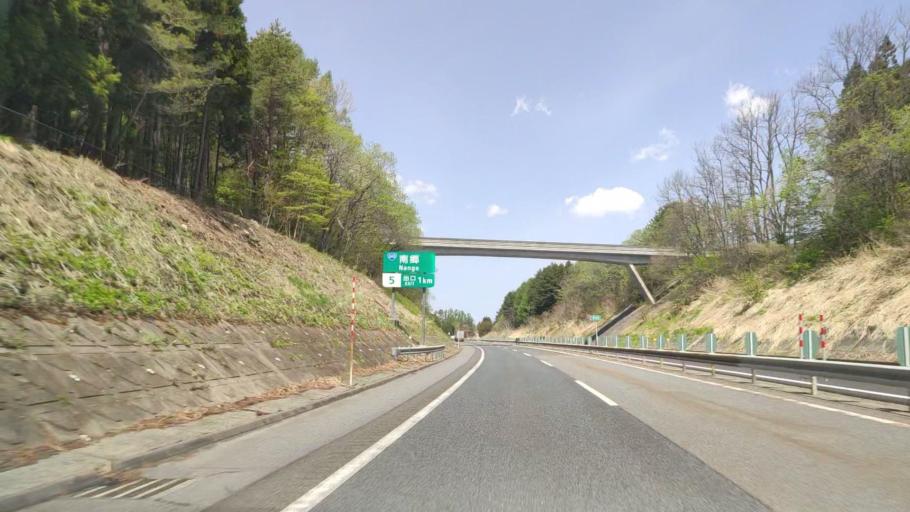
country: JP
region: Aomori
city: Hachinohe
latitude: 40.3968
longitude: 141.4476
